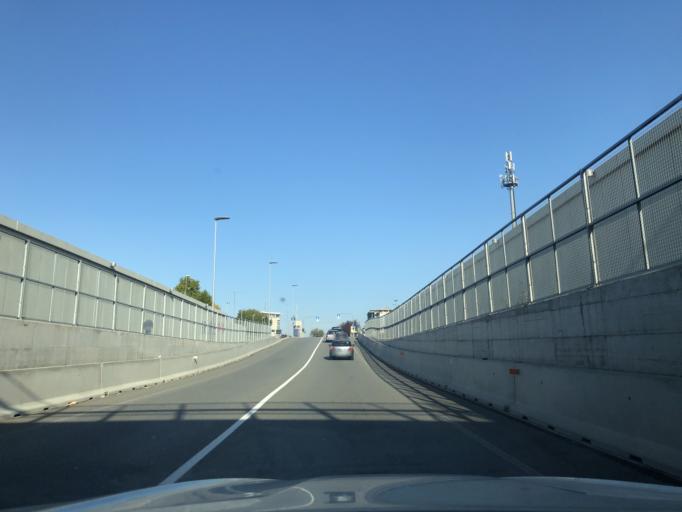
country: IT
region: Lombardy
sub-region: Citta metropolitana di Milano
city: Baranzate
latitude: 45.5304
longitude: 9.1095
